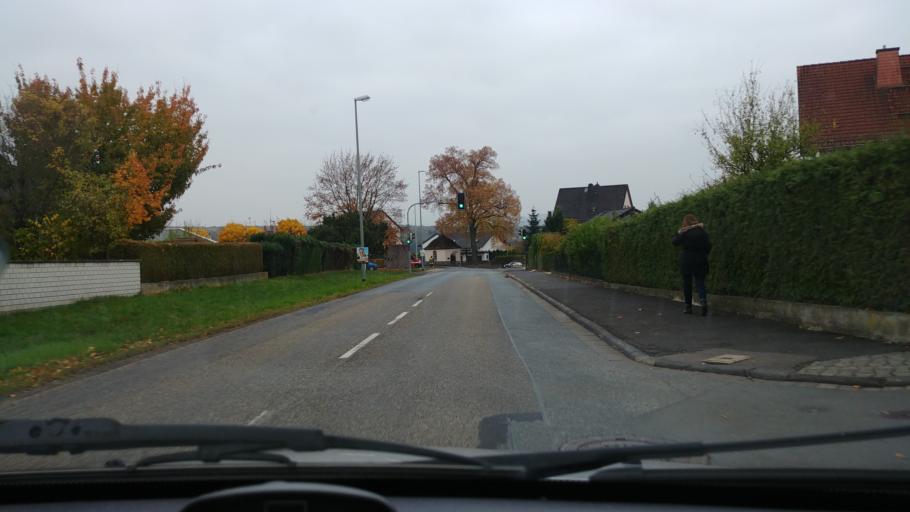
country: DE
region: Hesse
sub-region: Regierungsbezirk Giessen
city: Dehrn
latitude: 50.4228
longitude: 8.0974
